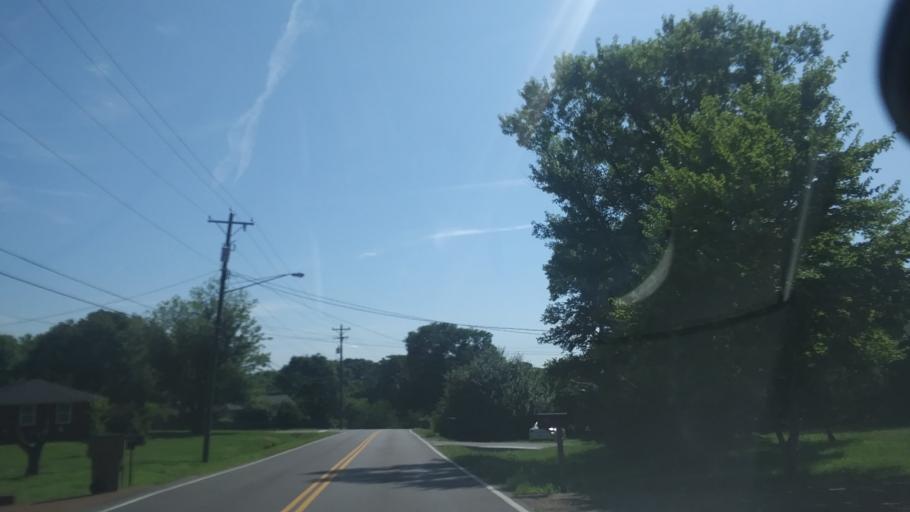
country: US
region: Tennessee
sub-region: Davidson County
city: Oak Hill
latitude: 36.0636
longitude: -86.6952
